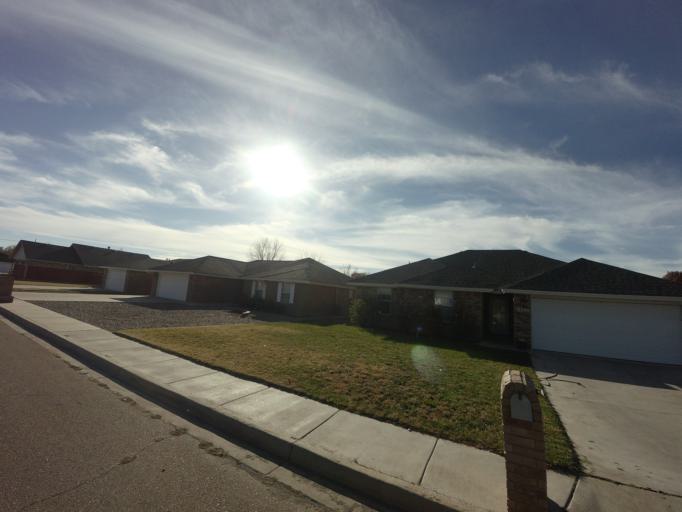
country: US
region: New Mexico
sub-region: Curry County
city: Clovis
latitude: 34.4137
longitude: -103.1754
